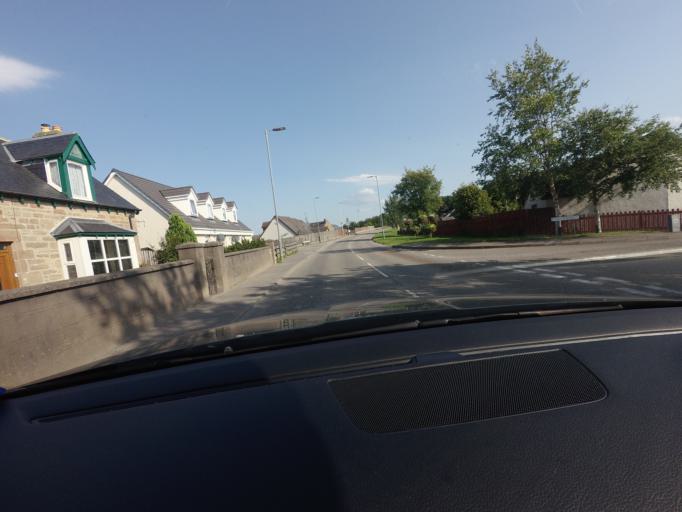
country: GB
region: Scotland
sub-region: Highland
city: Alness
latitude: 57.6948
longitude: -4.2462
